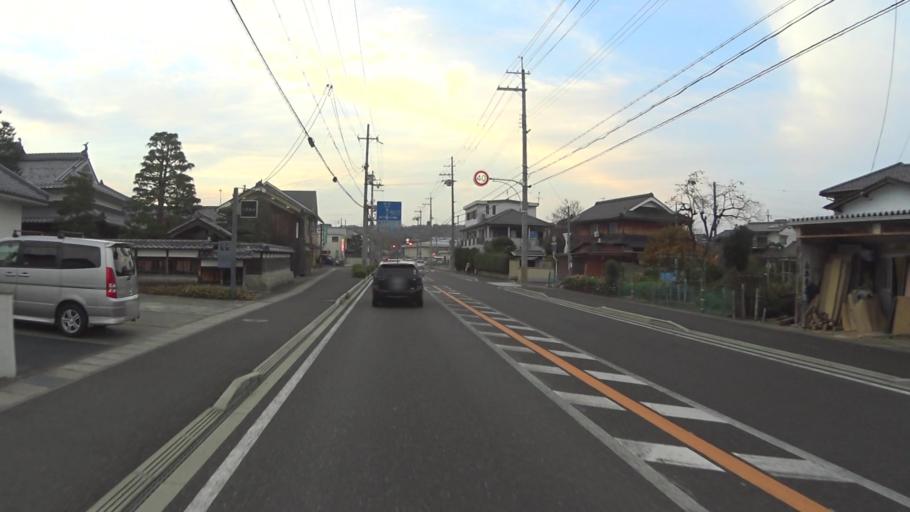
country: JP
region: Kyoto
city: Maizuru
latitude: 35.4612
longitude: 135.3994
